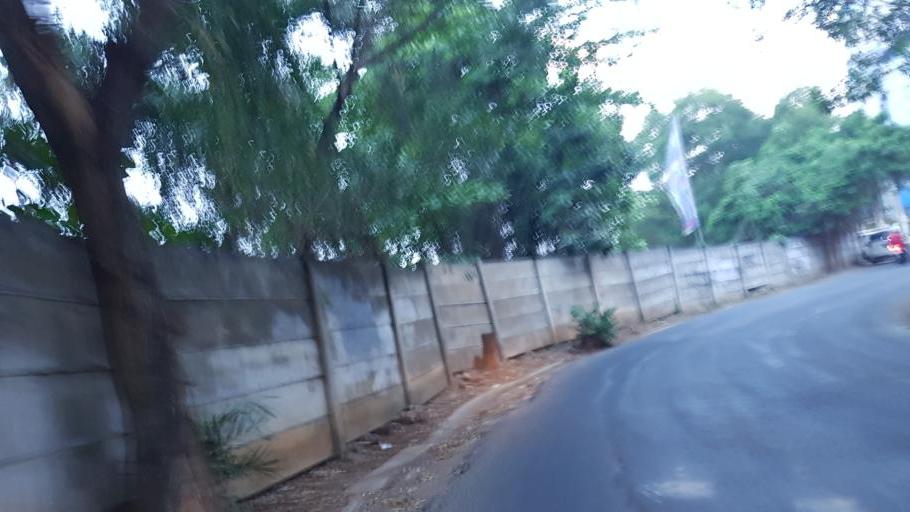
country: ID
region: West Java
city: Pamulang
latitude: -6.2951
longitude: 106.7972
